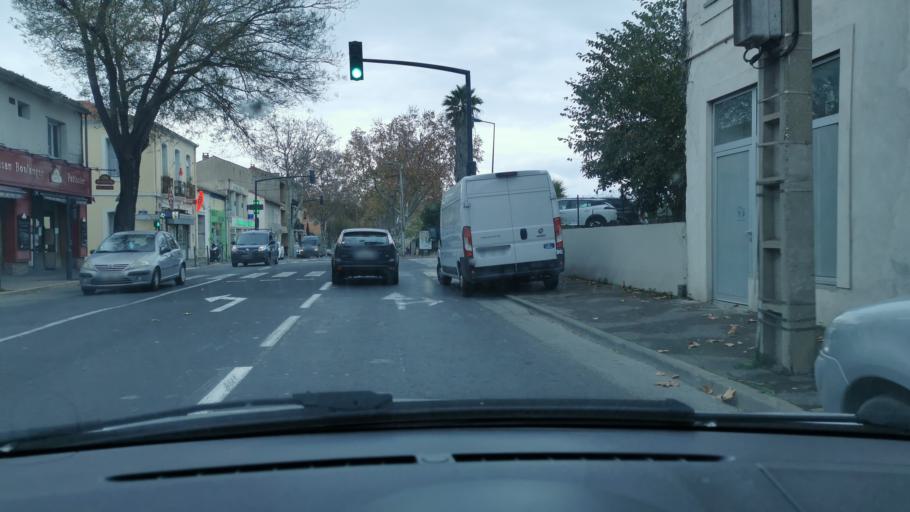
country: FR
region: Languedoc-Roussillon
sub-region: Departement de l'Herault
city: Sete
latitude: 43.4109
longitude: 3.6786
